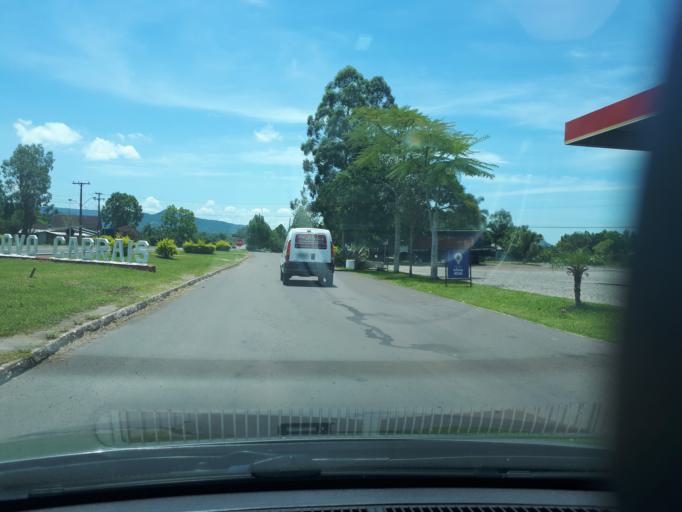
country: BR
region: Rio Grande do Sul
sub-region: Candelaria
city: Candelaria
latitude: -29.7325
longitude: -52.9469
